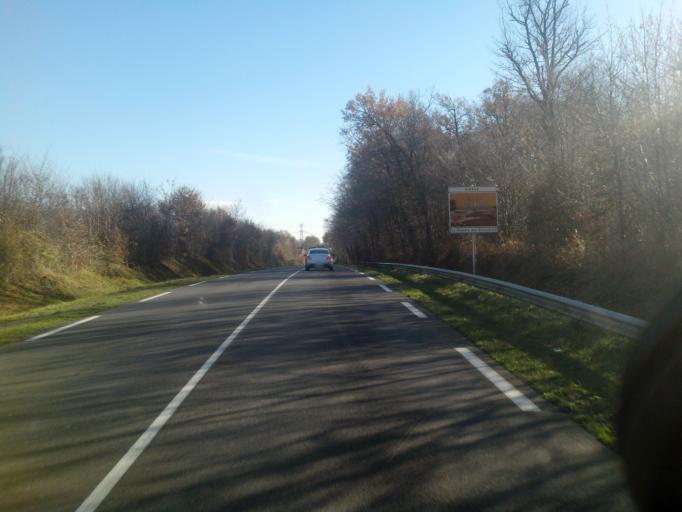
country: FR
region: Poitou-Charentes
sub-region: Departement de la Vienne
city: Lussac-les-Chateaux
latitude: 46.4253
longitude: 0.6254
